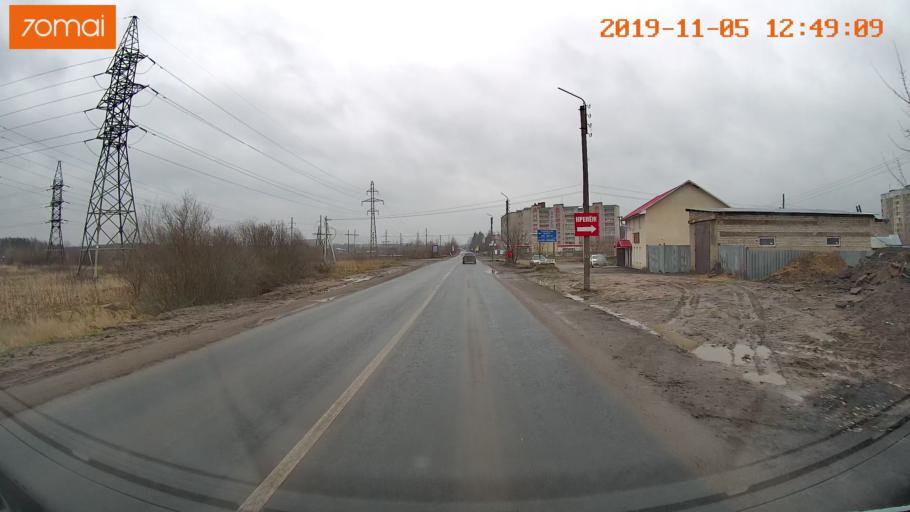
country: RU
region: Ivanovo
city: Kokhma
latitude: 56.9565
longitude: 41.1025
